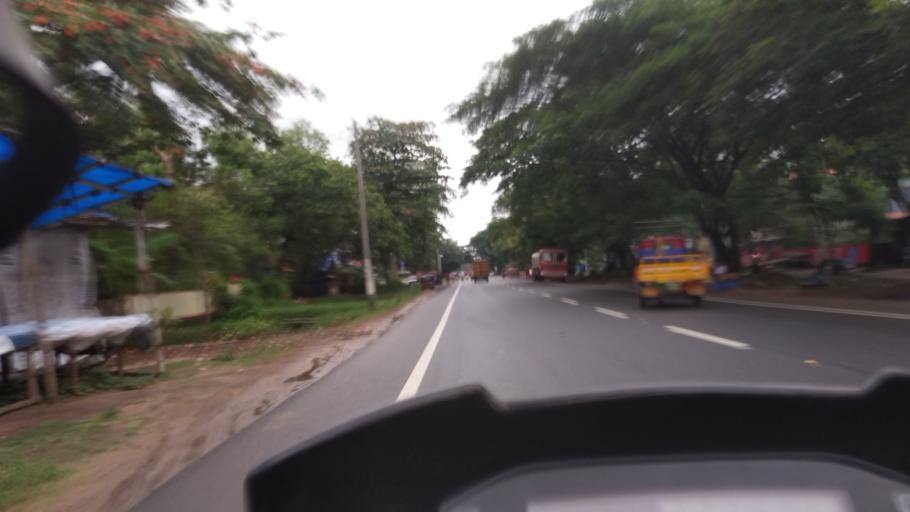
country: IN
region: Kerala
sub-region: Alappuzha
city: Mavelikara
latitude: 9.3131
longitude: 76.4292
